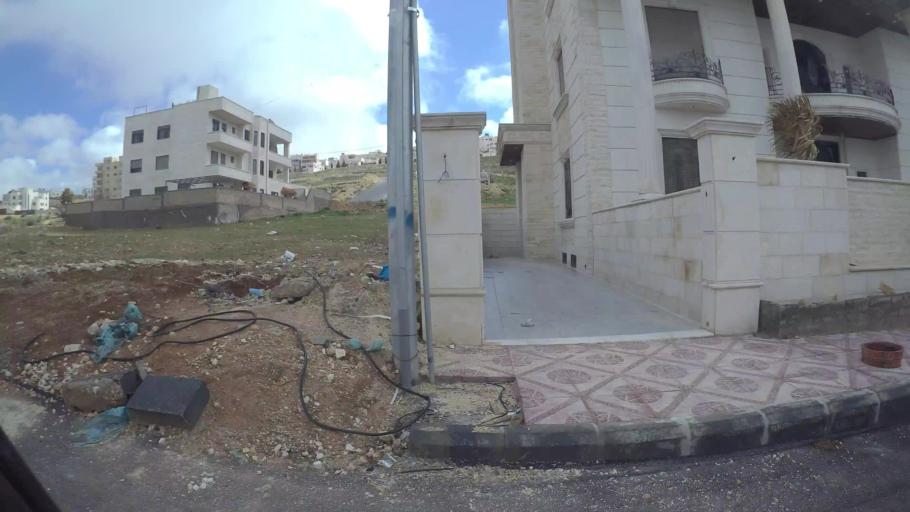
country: JO
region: Amman
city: Al Jubayhah
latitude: 32.0676
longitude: 35.8753
